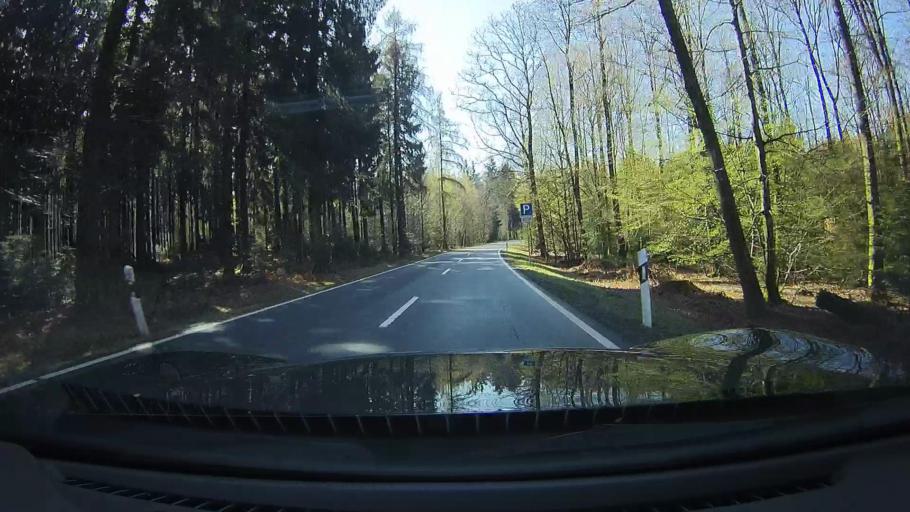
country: DE
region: Baden-Wuerttemberg
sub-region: Karlsruhe Region
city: Neunkirchen
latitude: 49.4209
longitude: 8.9829
